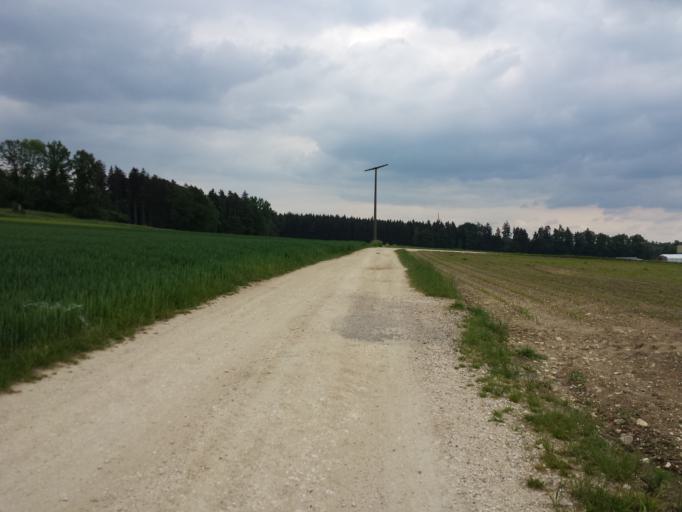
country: DE
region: Bavaria
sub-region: Swabia
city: Wasserburg
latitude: 48.4335
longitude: 10.3019
